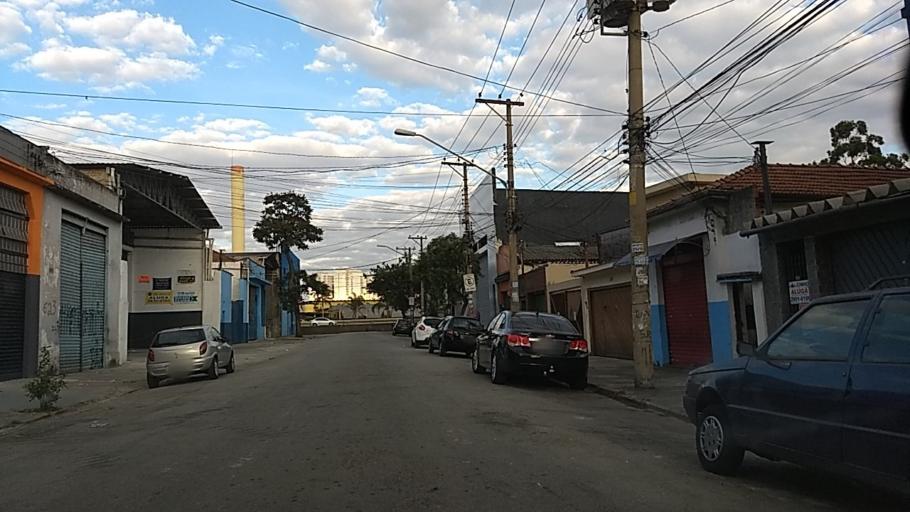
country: BR
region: Sao Paulo
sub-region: Sao Paulo
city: Sao Paulo
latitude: -23.5262
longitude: -46.5900
